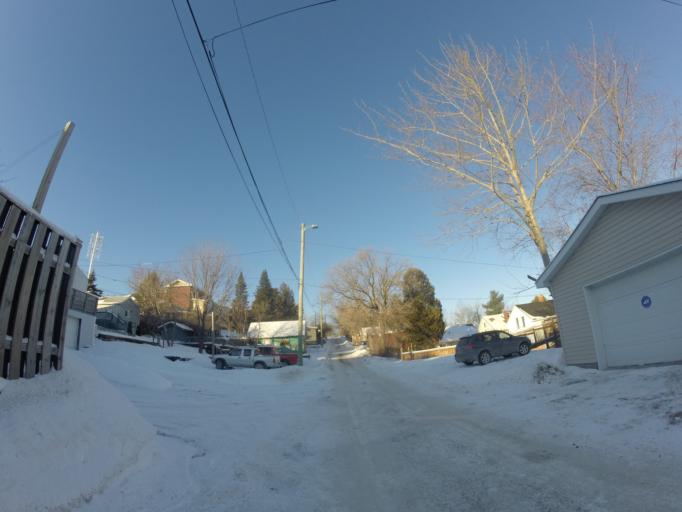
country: CA
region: Ontario
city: Greater Sudbury
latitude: 46.5028
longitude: -81.0000
